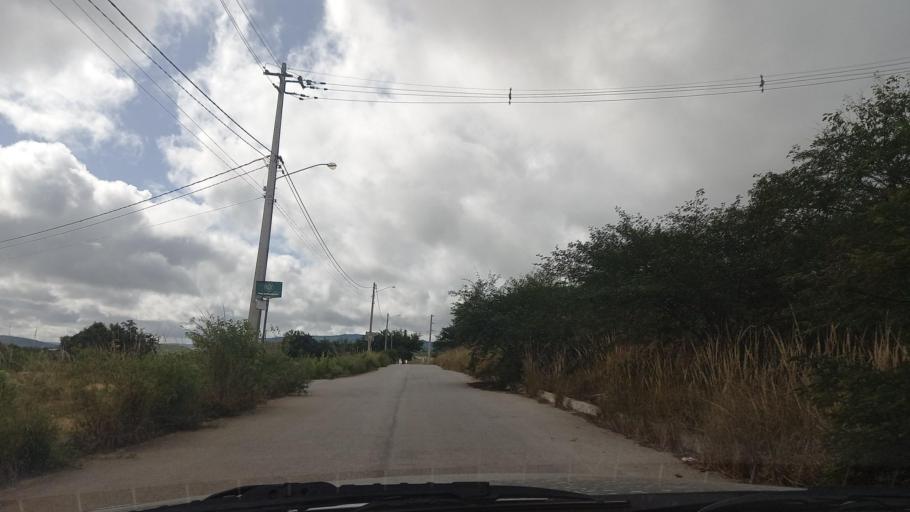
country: BR
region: Pernambuco
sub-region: Caruaru
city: Caruaru
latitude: -8.3070
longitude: -35.9584
